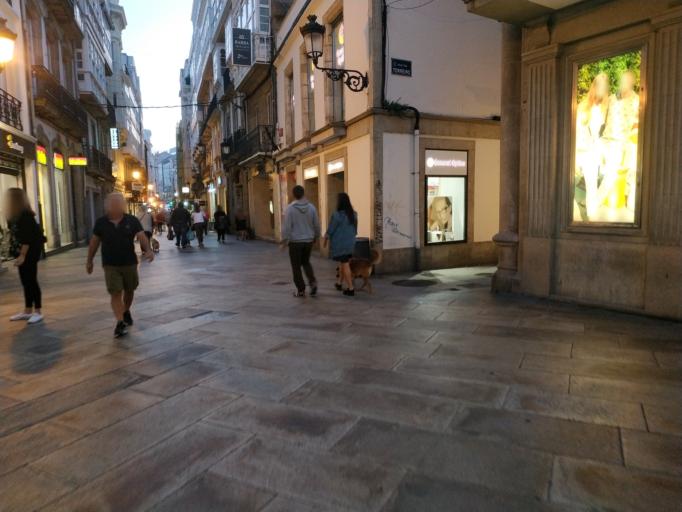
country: ES
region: Galicia
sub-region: Provincia da Coruna
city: A Coruna
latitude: 43.3704
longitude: -8.3991
